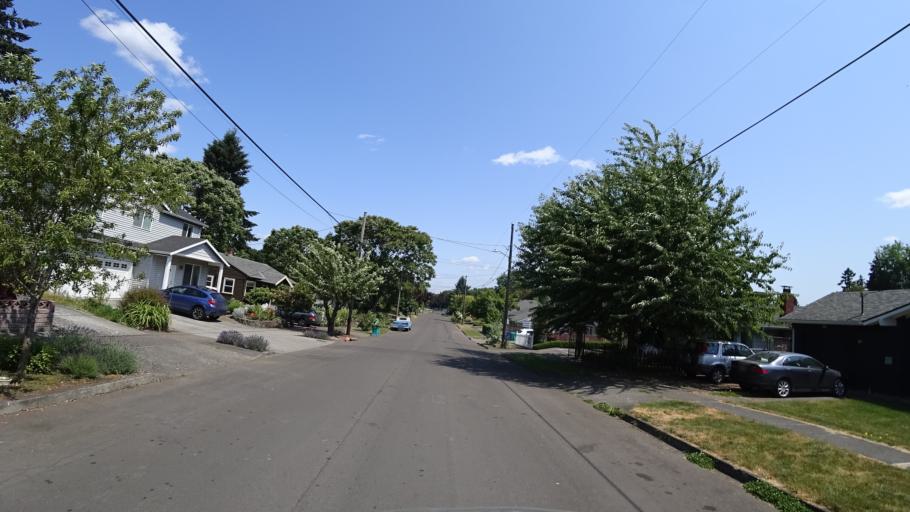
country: US
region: Oregon
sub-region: Washington County
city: West Haven
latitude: 45.5963
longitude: -122.7395
